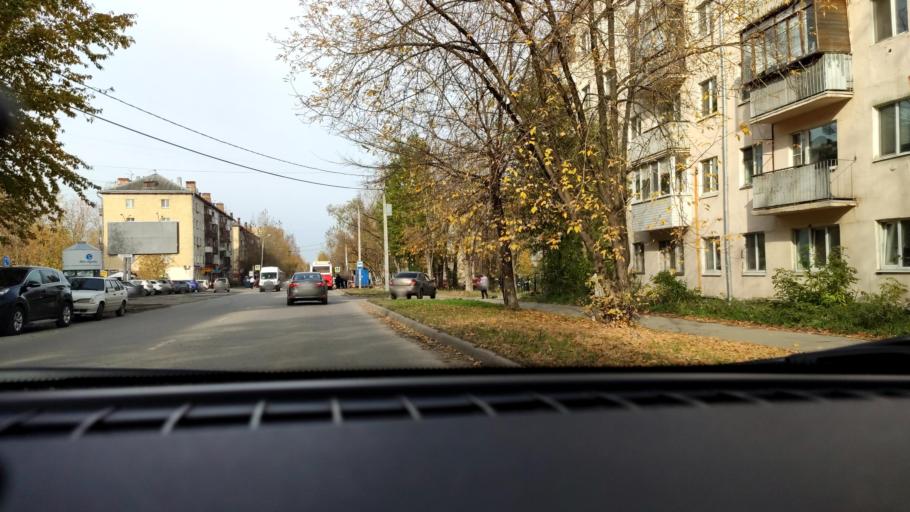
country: RU
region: Perm
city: Perm
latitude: 58.1033
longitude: 56.3872
